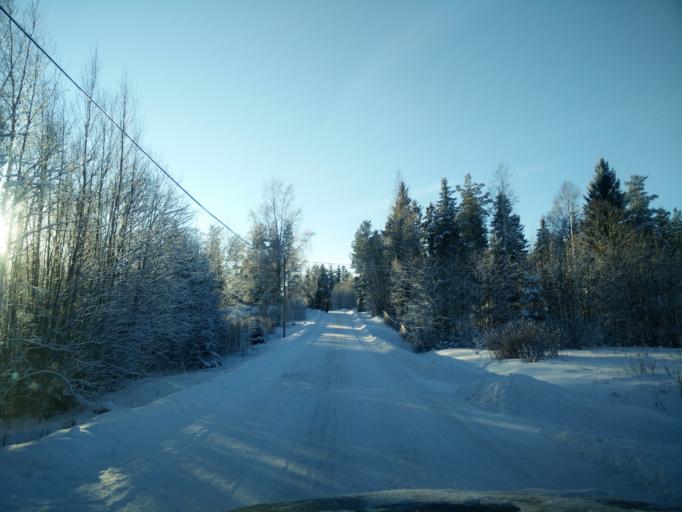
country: SE
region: Vaesternorrland
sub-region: Sundsvalls Kommun
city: Njurundabommen
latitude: 62.2291
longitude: 17.5007
